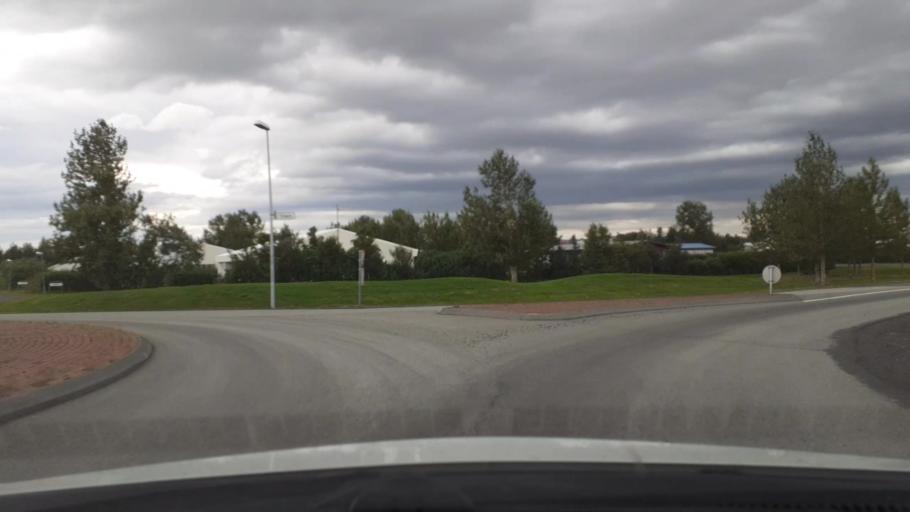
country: IS
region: West
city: Borgarnes
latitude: 64.5606
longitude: -21.7620
